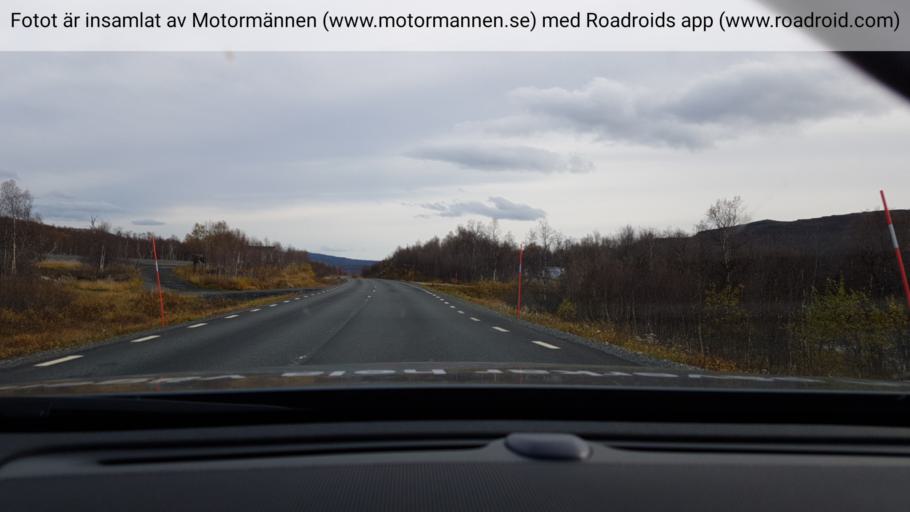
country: NO
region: Nordland
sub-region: Sorfold
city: Straumen
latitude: 66.6104
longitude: 16.2488
